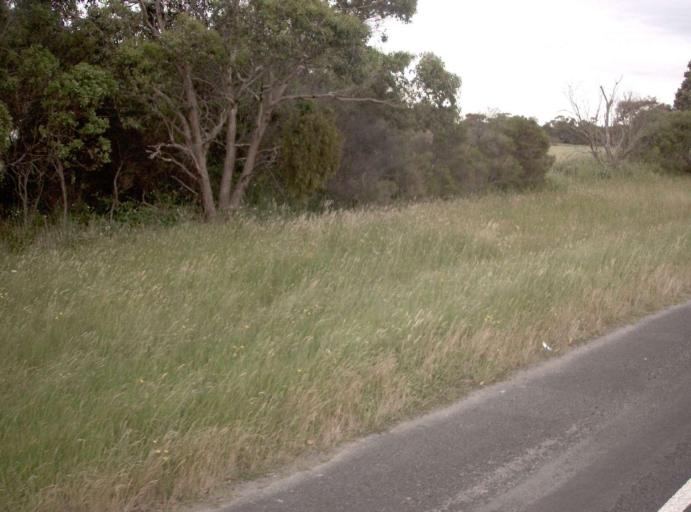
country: AU
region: Victoria
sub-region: Casey
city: Blind Bight
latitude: -38.1855
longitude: 145.3439
